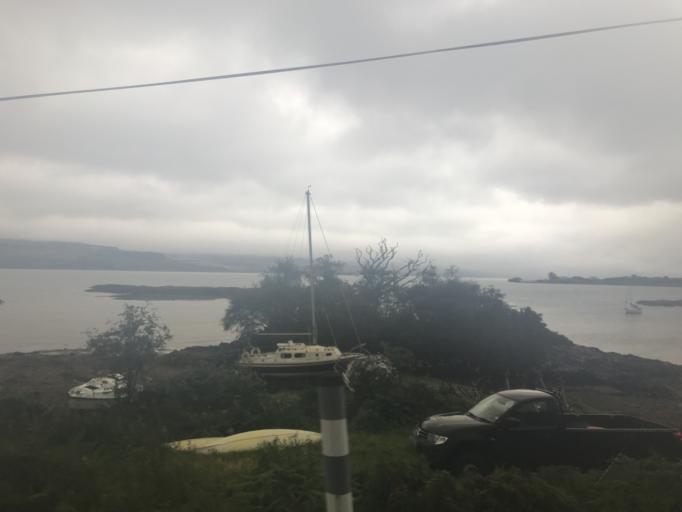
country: GB
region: Scotland
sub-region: Argyll and Bute
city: Isle Of Mull
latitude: 56.5236
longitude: -5.9578
